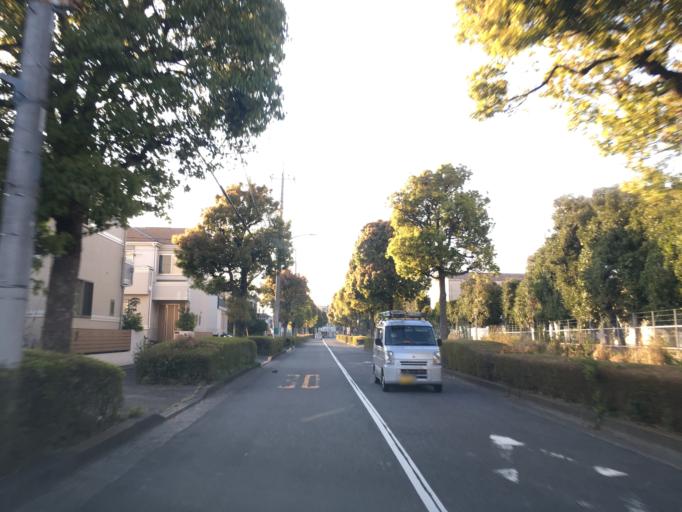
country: JP
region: Tokyo
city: Kokubunji
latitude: 35.6662
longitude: 139.4531
